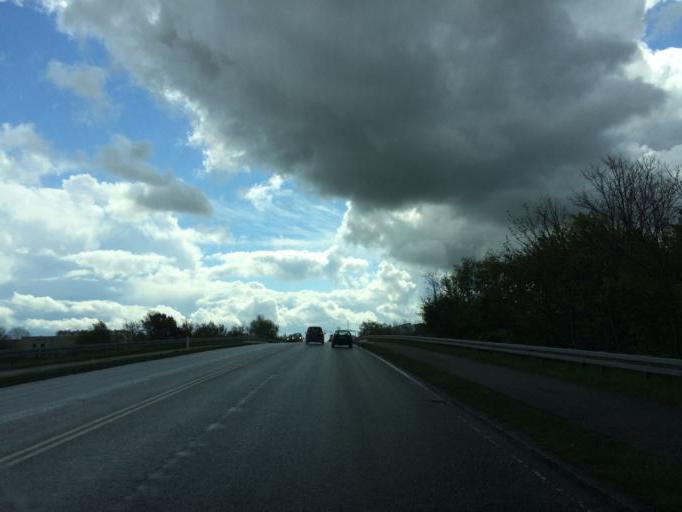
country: DK
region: Central Jutland
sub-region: Holstebro Kommune
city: Holstebro
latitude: 56.3751
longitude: 8.6209
